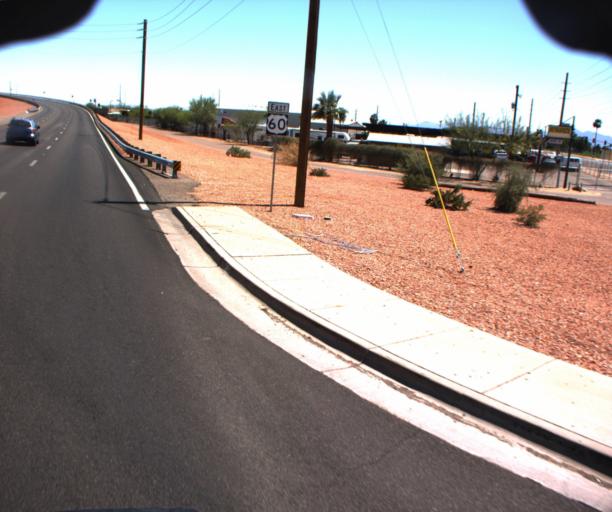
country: US
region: Arizona
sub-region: Maricopa County
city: Peoria
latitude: 33.5661
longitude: -112.2200
